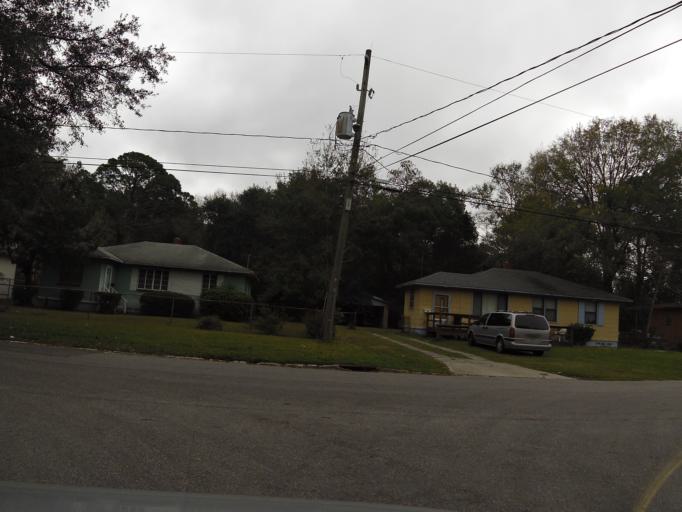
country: US
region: Florida
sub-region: Duval County
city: Jacksonville
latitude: 30.3732
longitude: -81.7044
